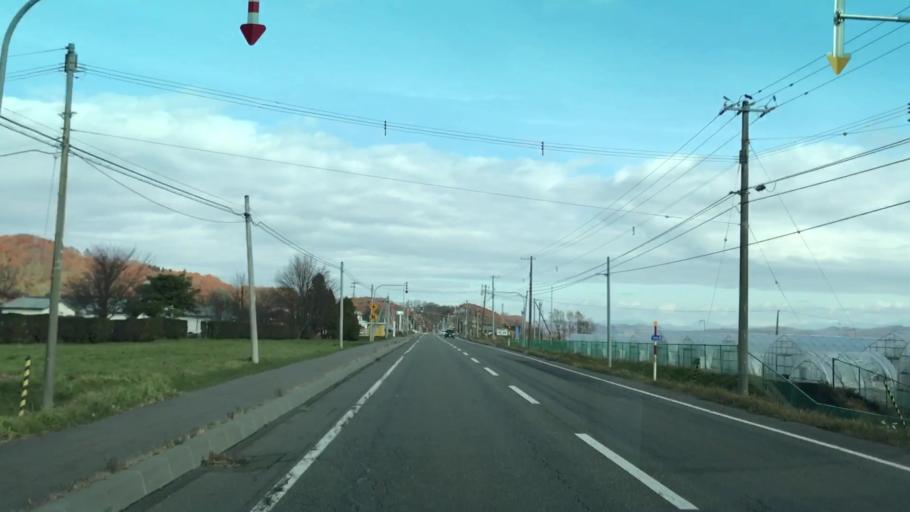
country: JP
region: Hokkaido
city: Shizunai-furukawacho
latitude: 42.5546
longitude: 142.0759
